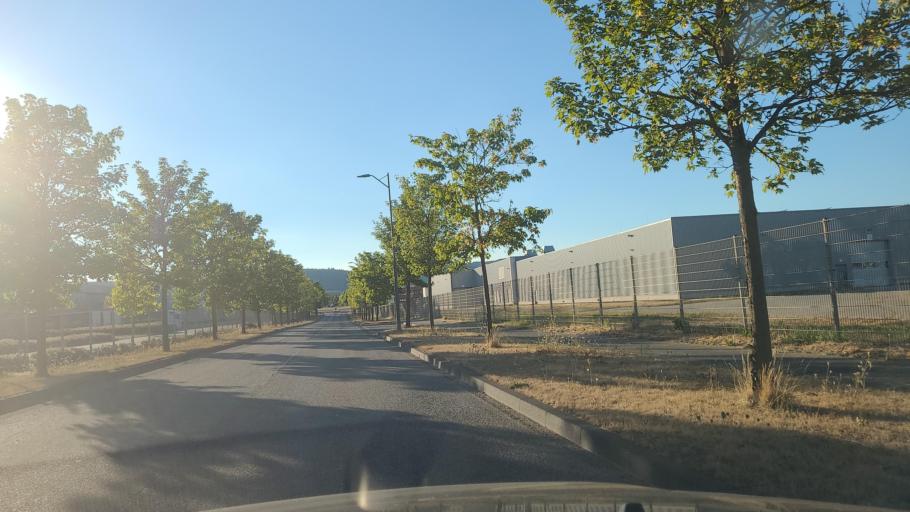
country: DE
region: Rheinland-Pfalz
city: Bekond
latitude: 49.8580
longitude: 6.7977
